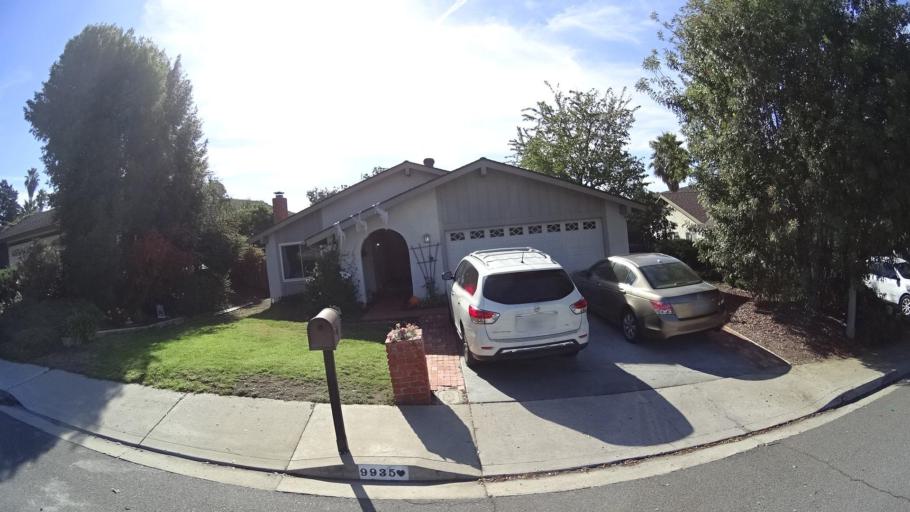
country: US
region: California
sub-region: San Diego County
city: Spring Valley
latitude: 32.7282
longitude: -116.9819
